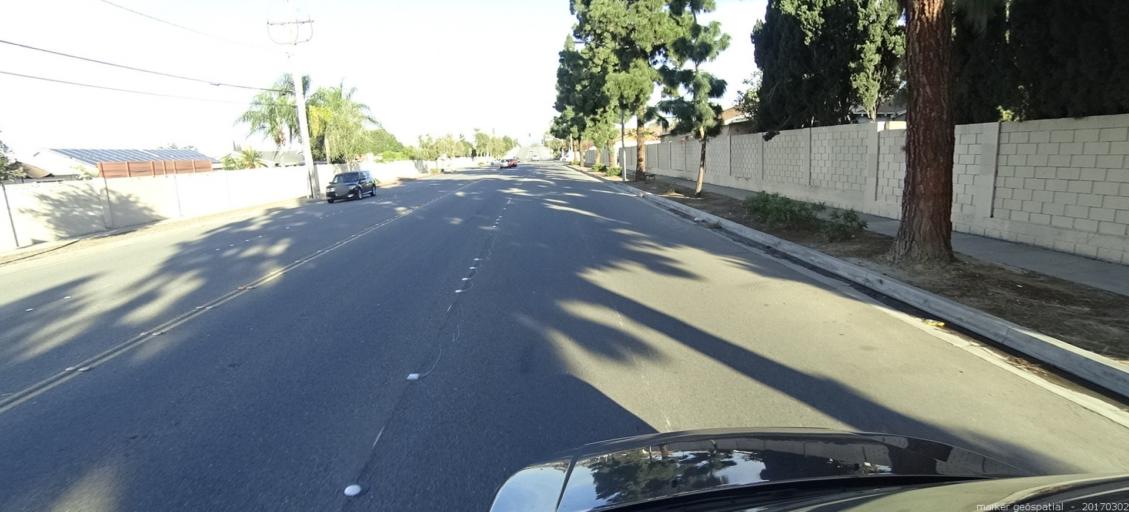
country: US
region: California
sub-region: Orange County
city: Anaheim
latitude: 33.8253
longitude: -117.8820
